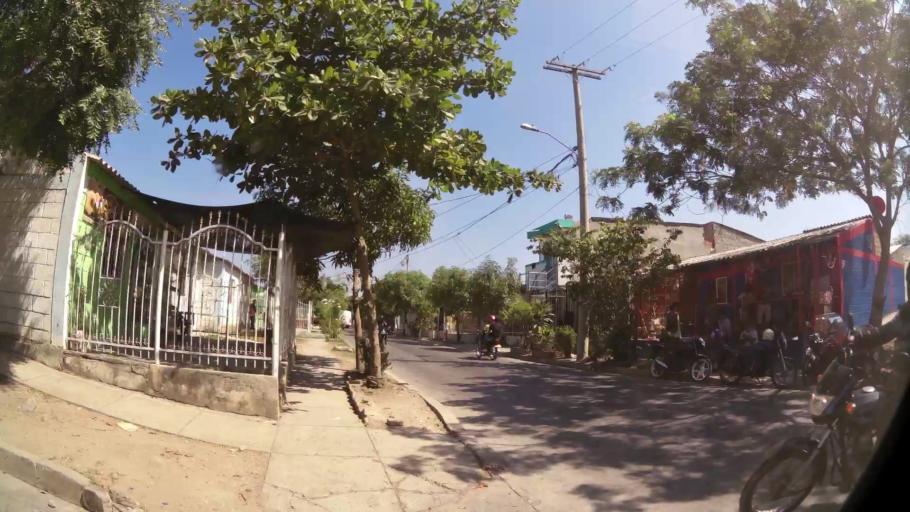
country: CO
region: Bolivar
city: Cartagena
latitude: 10.3909
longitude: -75.4530
